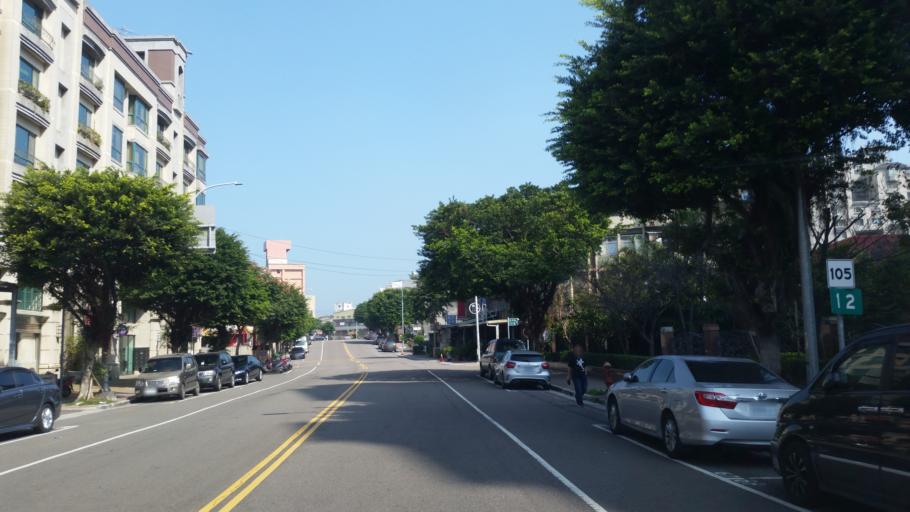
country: TW
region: Taipei
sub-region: Taipei
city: Banqiao
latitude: 25.0800
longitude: 121.3856
